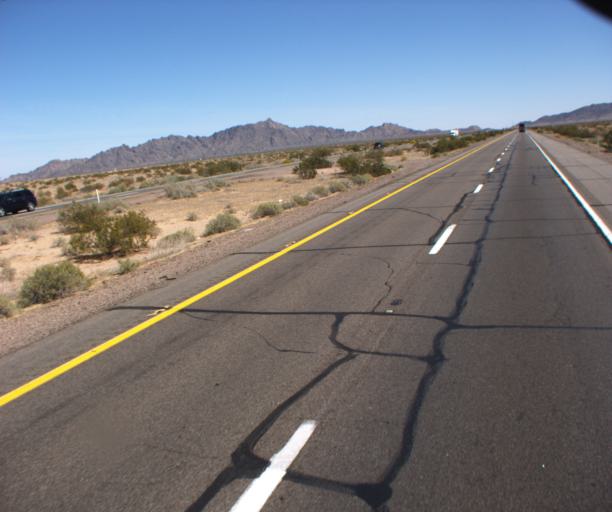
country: US
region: Arizona
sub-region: Yuma County
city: Wellton
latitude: 32.7113
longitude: -113.8353
